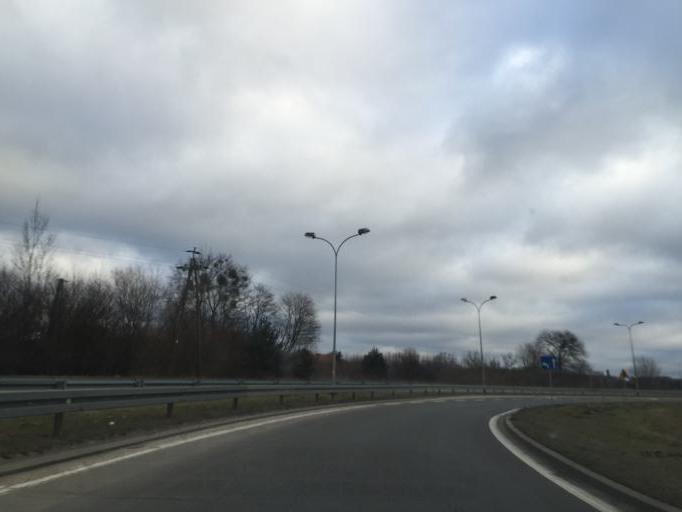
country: PL
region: Pomeranian Voivodeship
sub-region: Gdynia
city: Wielki Kack
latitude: 54.4130
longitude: 18.4885
